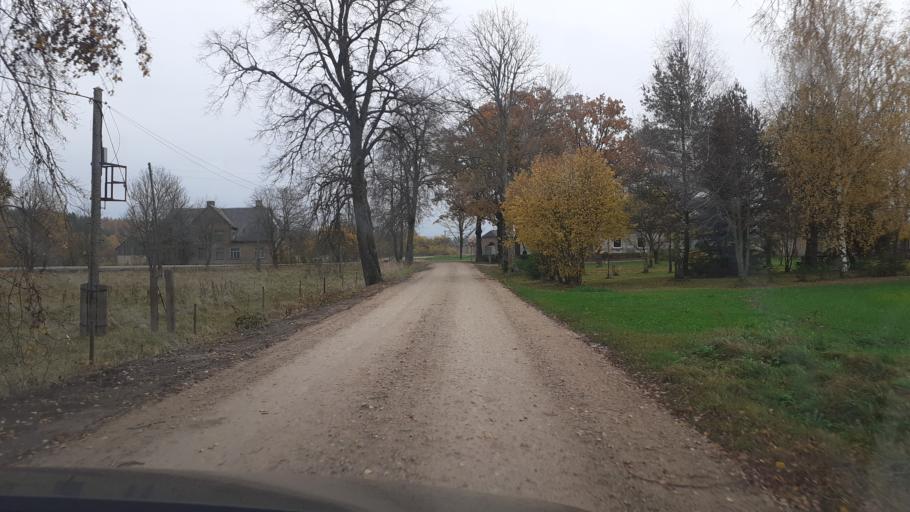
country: LV
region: Skrunda
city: Skrunda
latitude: 56.8575
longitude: 22.2293
